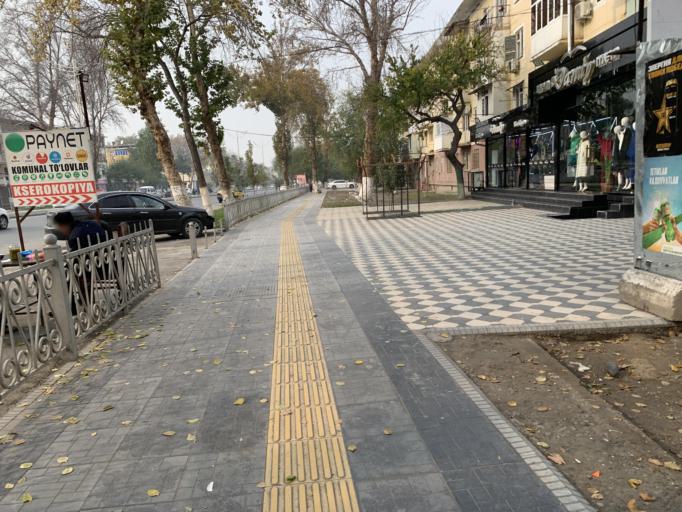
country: UZ
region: Fergana
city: Qo`qon
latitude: 40.5444
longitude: 70.9331
